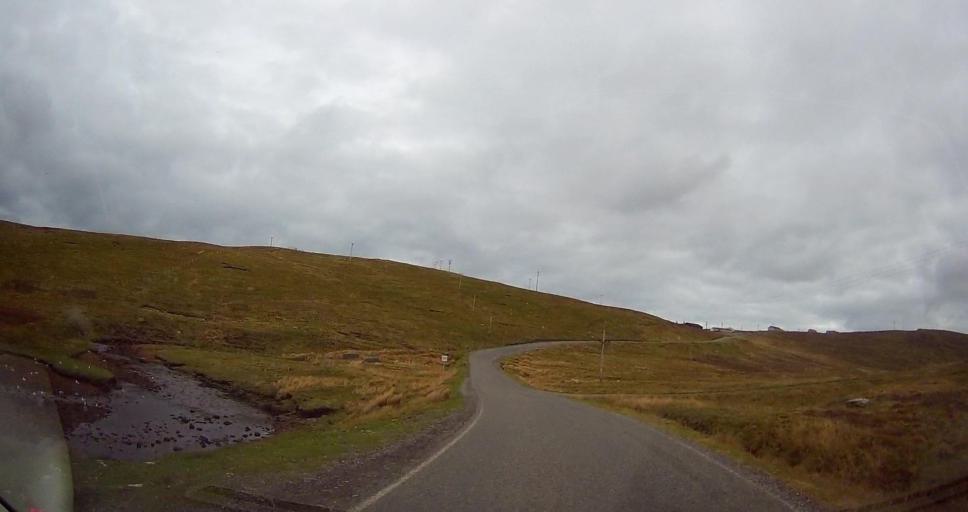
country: GB
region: Scotland
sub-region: Shetland Islands
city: Shetland
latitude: 60.6032
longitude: -1.0842
